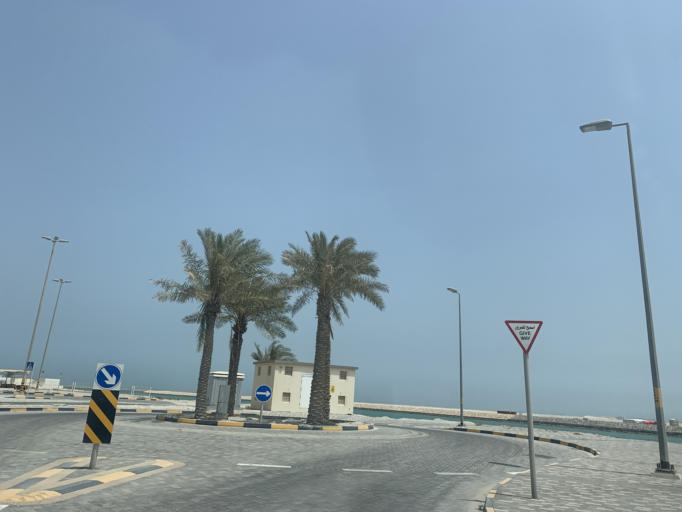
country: BH
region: Muharraq
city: Al Hadd
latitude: 26.2681
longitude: 50.6724
